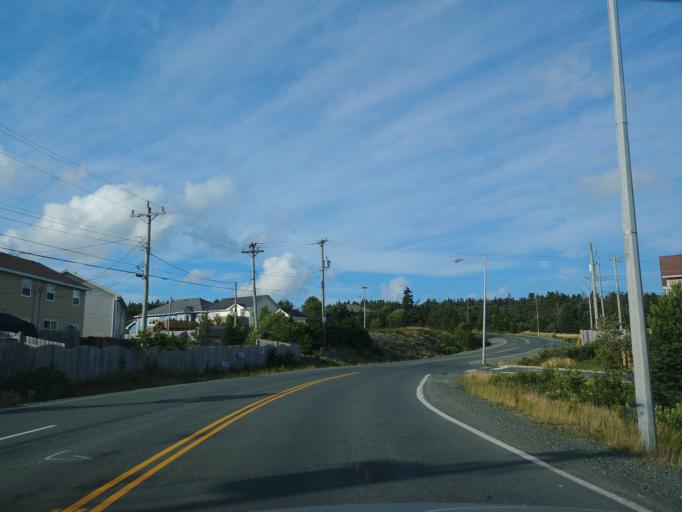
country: CA
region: Newfoundland and Labrador
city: Mount Pearl
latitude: 47.5649
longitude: -52.7633
